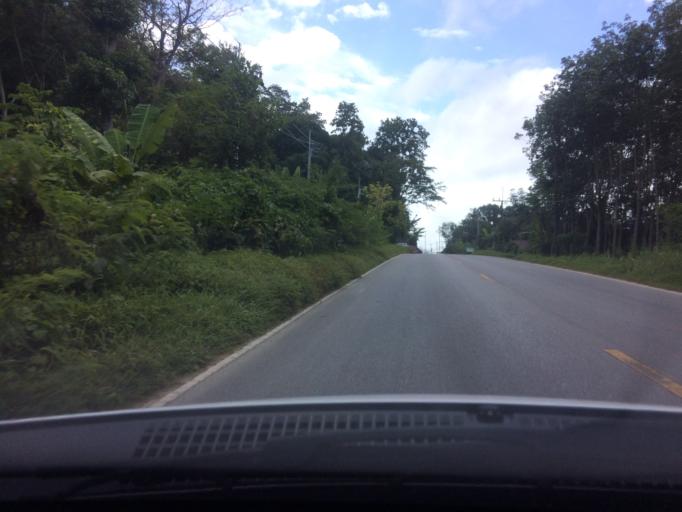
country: TH
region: Phuket
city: Thalang
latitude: 8.0874
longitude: 98.3648
